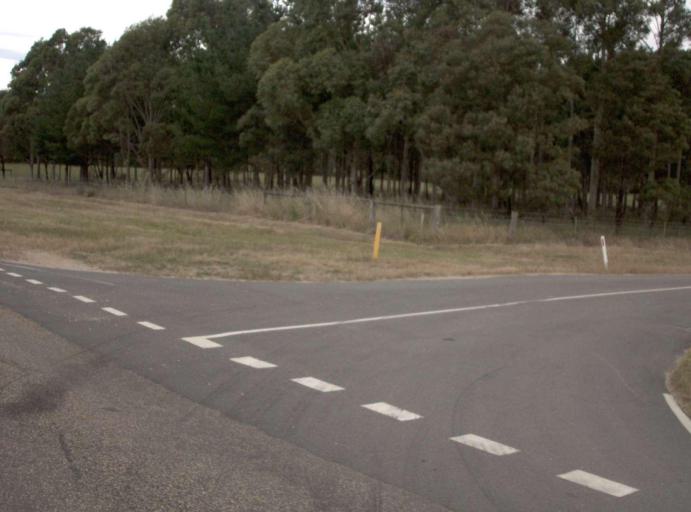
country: AU
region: Victoria
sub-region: Wellington
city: Sale
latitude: -38.0032
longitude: 147.2566
